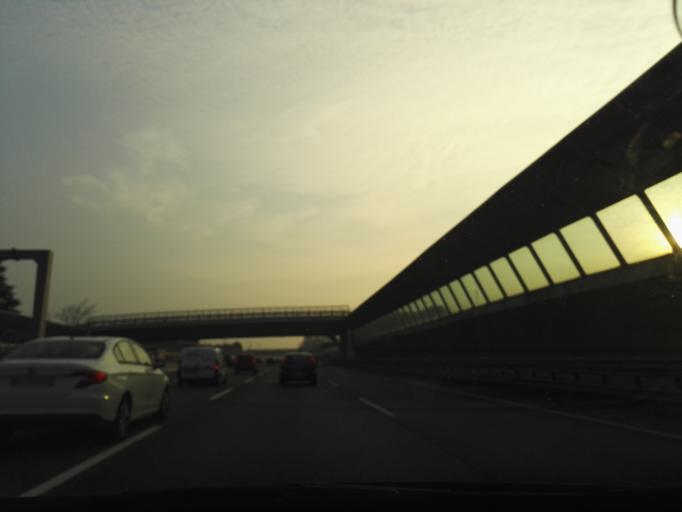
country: IT
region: Lombardy
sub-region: Citta metropolitana di Milano
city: Trezzo sull'Adda
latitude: 45.6005
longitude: 9.5157
